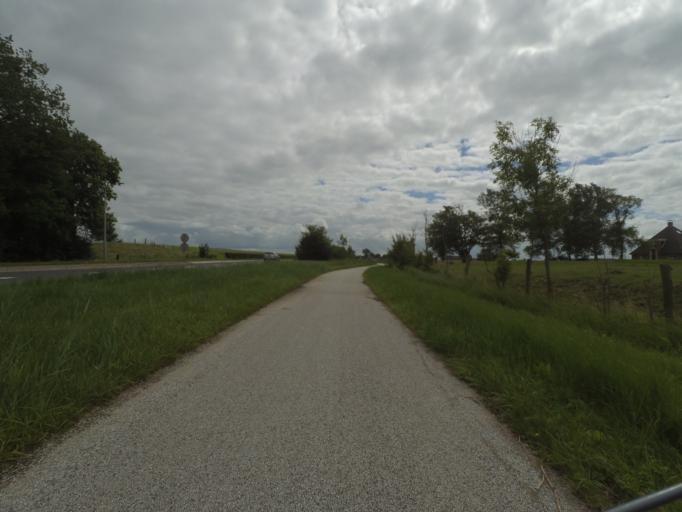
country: NL
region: Friesland
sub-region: Gemeente Kollumerland en Nieuwkruisland
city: Kollum
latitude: 53.3244
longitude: 6.1523
